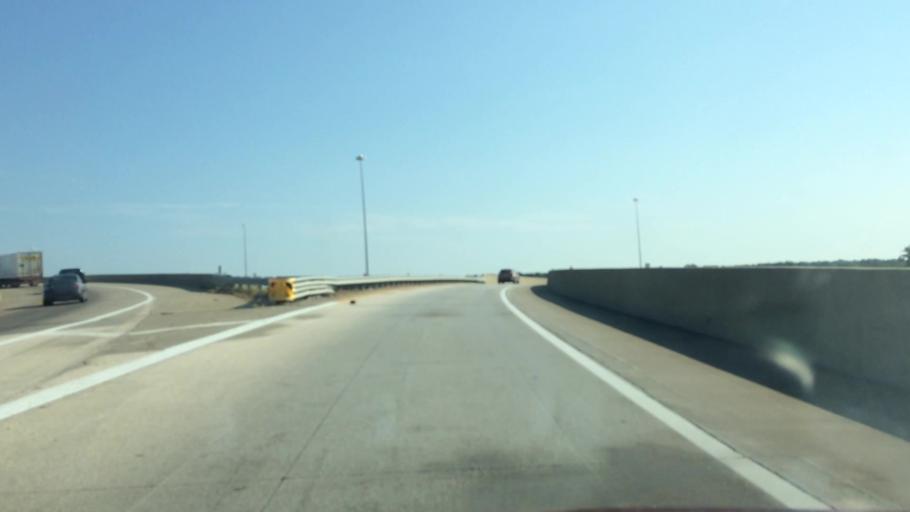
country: US
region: Missouri
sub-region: Greene County
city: Springfield
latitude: 37.2479
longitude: -93.2239
